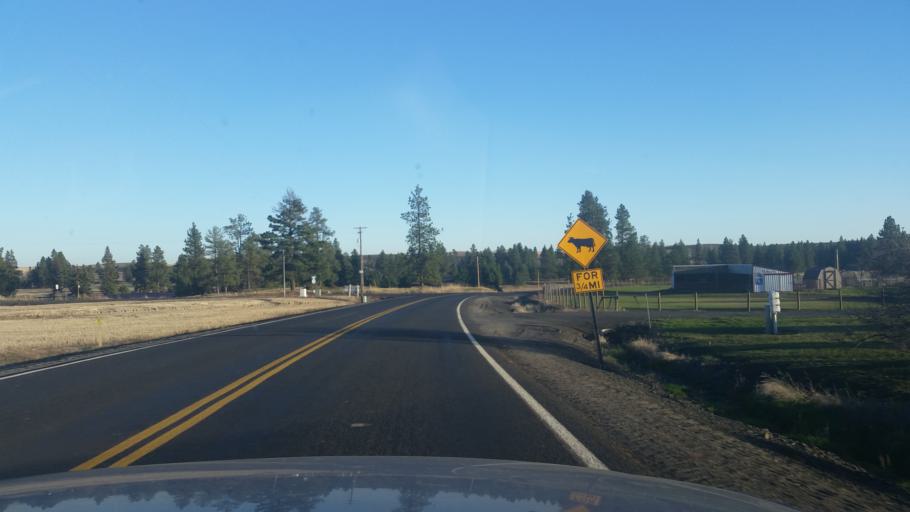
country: US
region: Washington
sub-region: Spokane County
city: Opportunity
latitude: 47.3845
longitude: -117.3177
